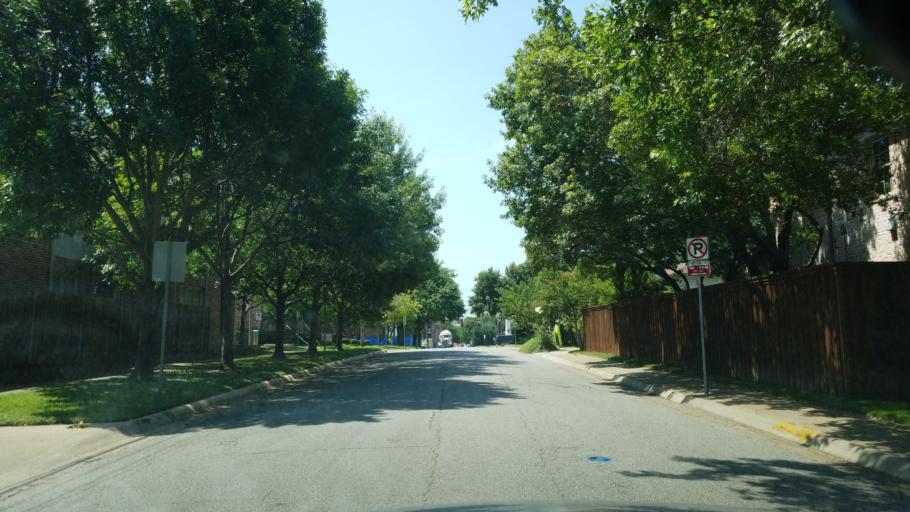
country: US
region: Texas
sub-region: Dallas County
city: Highland Park
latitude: 32.8484
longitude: -96.7829
